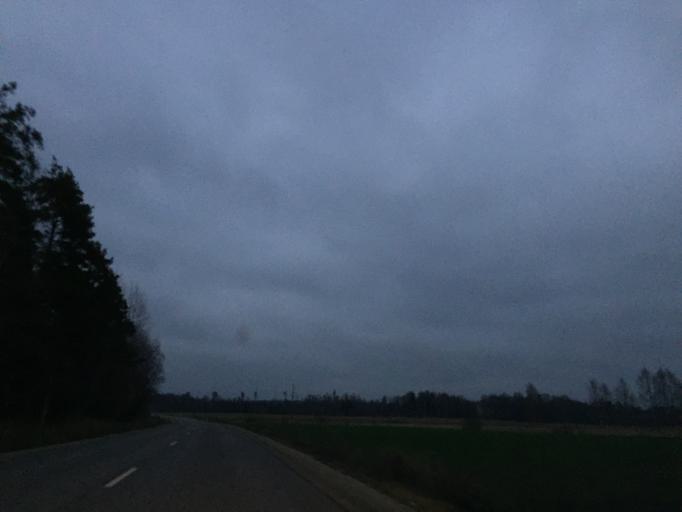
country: LV
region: Koceni
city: Koceni
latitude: 57.5508
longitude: 25.3443
